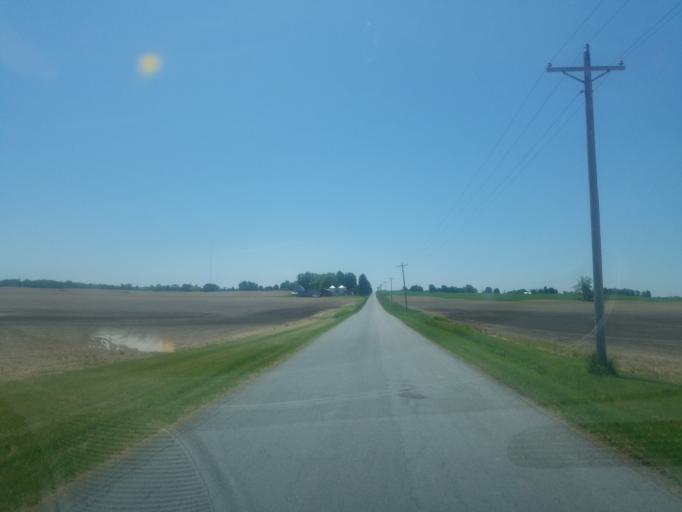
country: US
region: Ohio
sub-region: Huron County
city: New London
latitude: 41.1004
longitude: -82.4625
